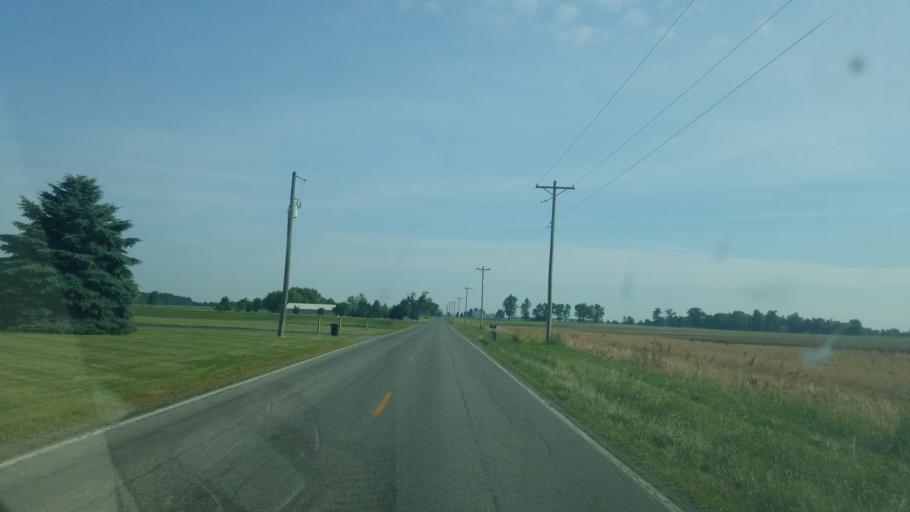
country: US
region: Ohio
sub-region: Hancock County
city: Arlington
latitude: 40.9445
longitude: -83.6987
